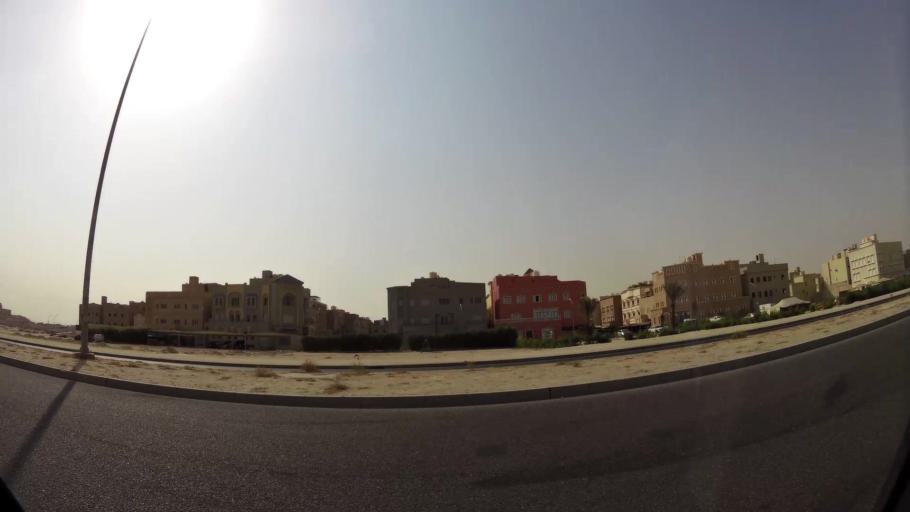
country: KW
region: Muhafazat al Jahra'
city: Al Jahra'
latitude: 29.3420
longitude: 47.7661
